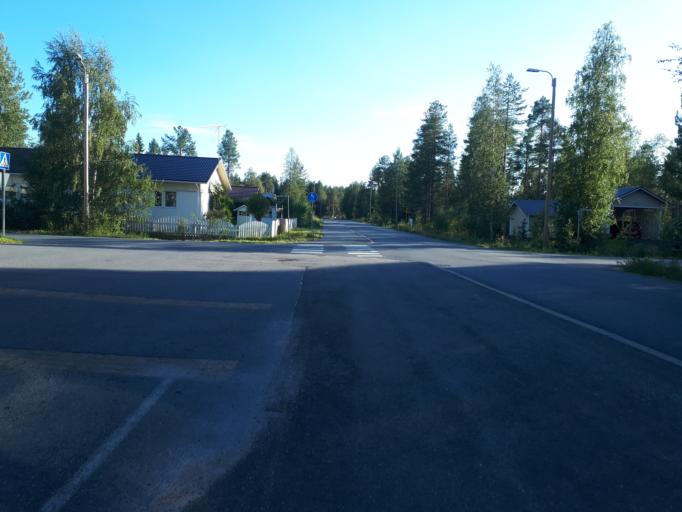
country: FI
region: Northern Ostrobothnia
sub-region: Oulunkaari
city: Ii
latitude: 65.3145
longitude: 25.3856
